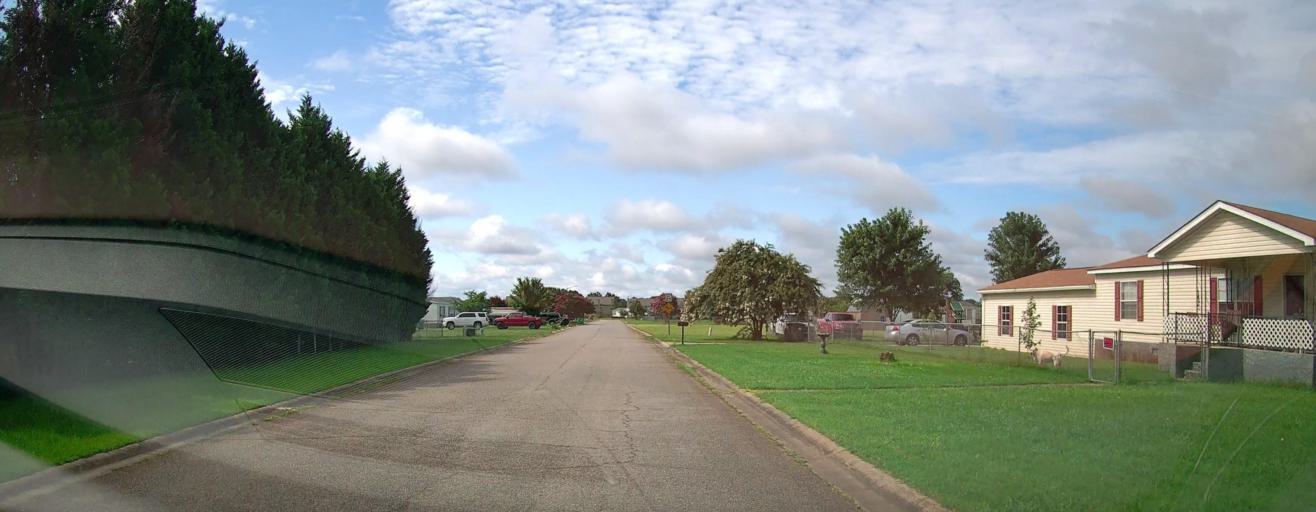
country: US
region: Georgia
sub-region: Houston County
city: Centerville
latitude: 32.6483
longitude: -83.7143
